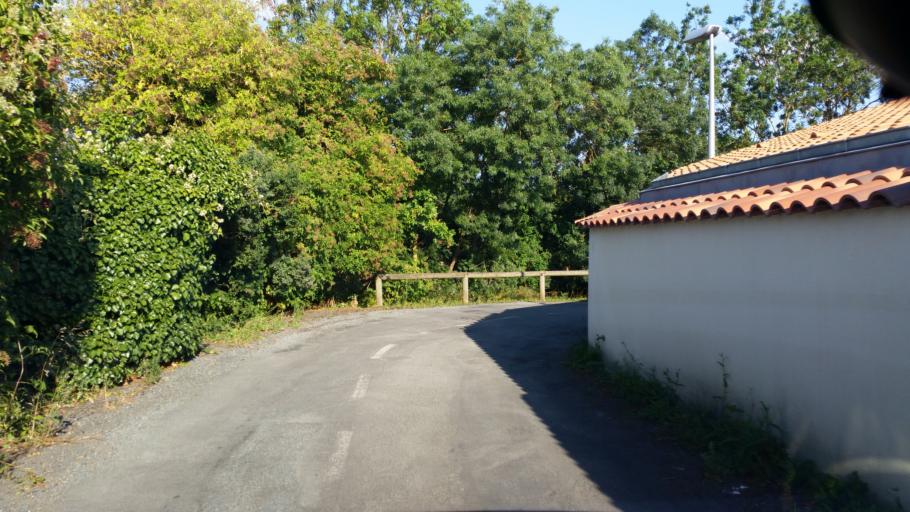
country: FR
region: Poitou-Charentes
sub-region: Departement de la Charente-Maritime
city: Marans
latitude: 46.3080
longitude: -0.9856
